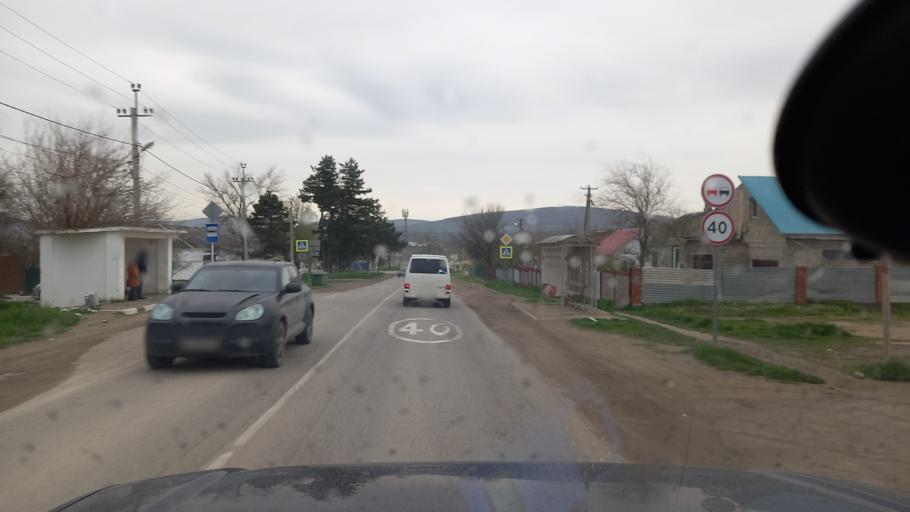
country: RU
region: Krasnodarskiy
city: Anapskaya
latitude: 44.8934
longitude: 37.4596
